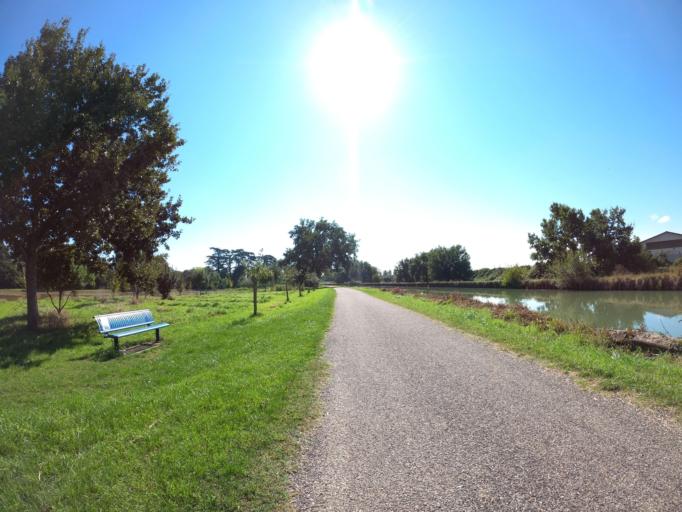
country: FR
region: Aquitaine
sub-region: Departement du Lot-et-Garonne
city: Bon-Encontre
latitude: 44.1750
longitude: 0.6661
